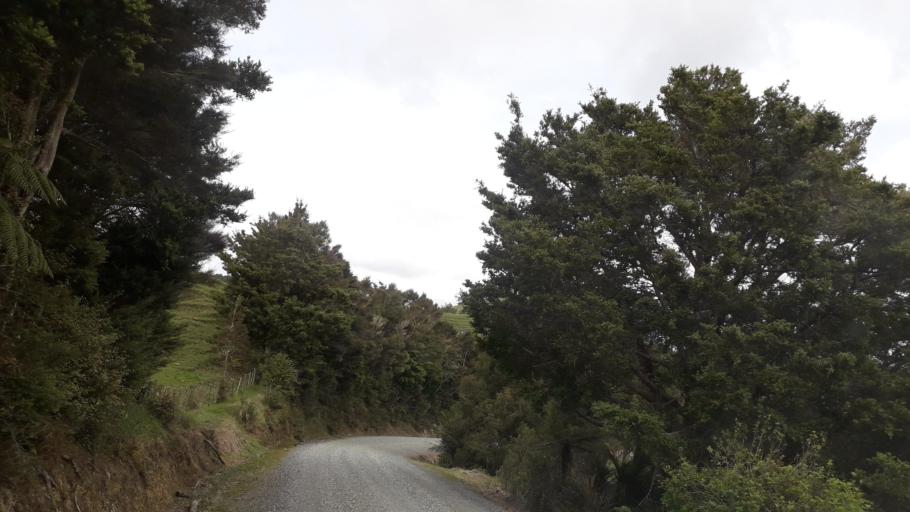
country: NZ
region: Northland
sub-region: Far North District
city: Waimate North
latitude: -35.1408
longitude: 173.7135
